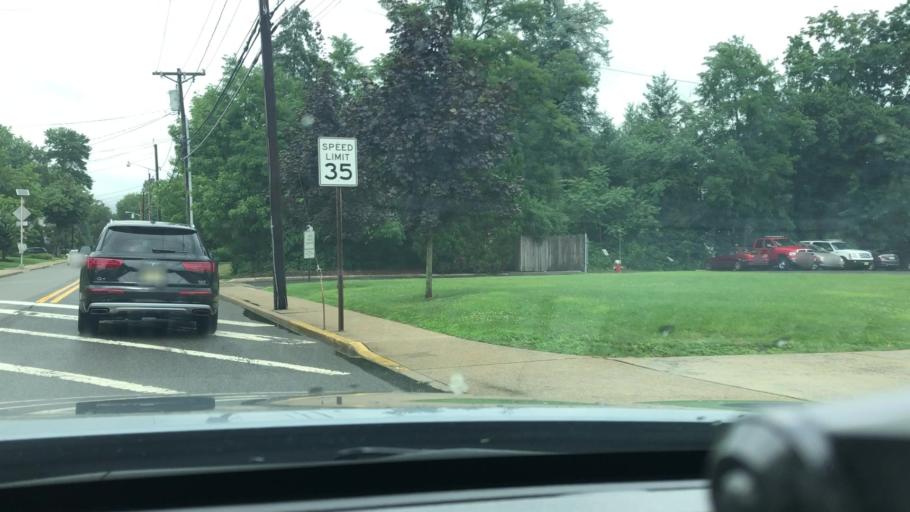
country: US
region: New Jersey
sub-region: Bergen County
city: Ho-Ho-Kus
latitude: 40.9990
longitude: -74.1097
